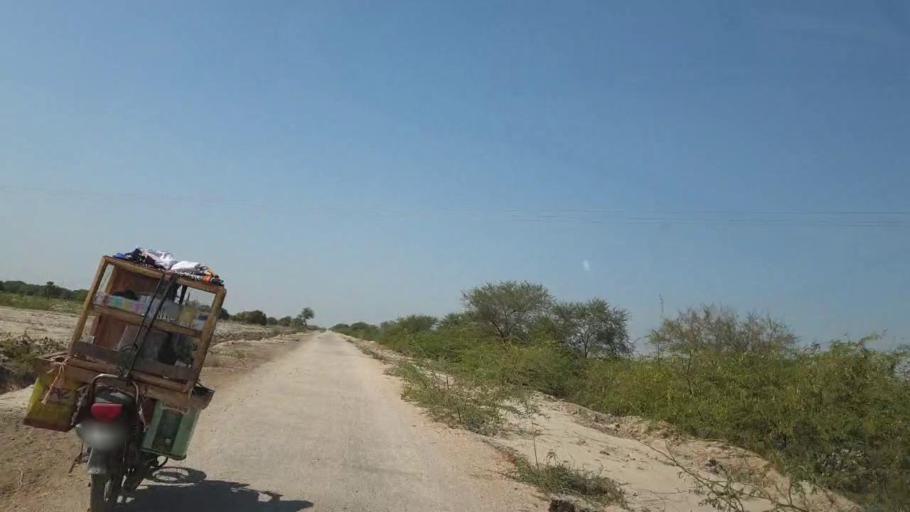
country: PK
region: Sindh
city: Kunri
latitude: 25.0963
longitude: 69.5223
